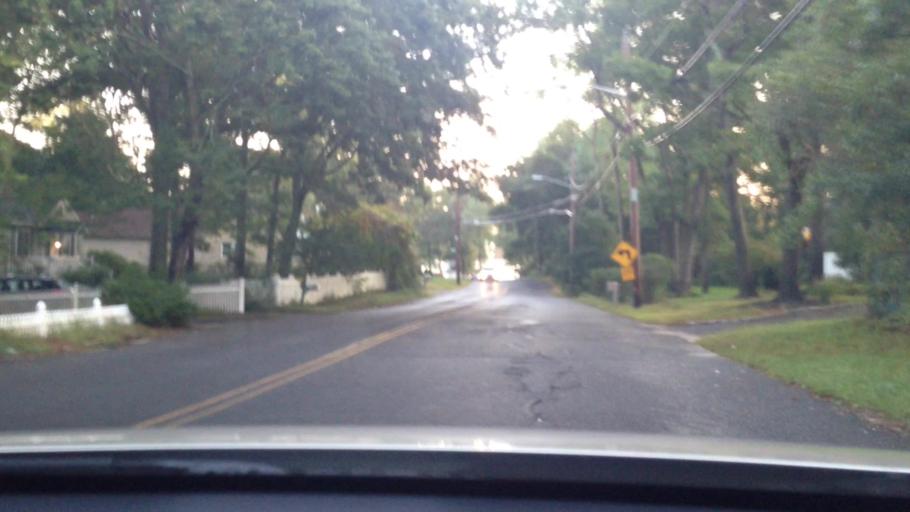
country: US
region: New York
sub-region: Suffolk County
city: Selden
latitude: 40.8492
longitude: -73.0337
